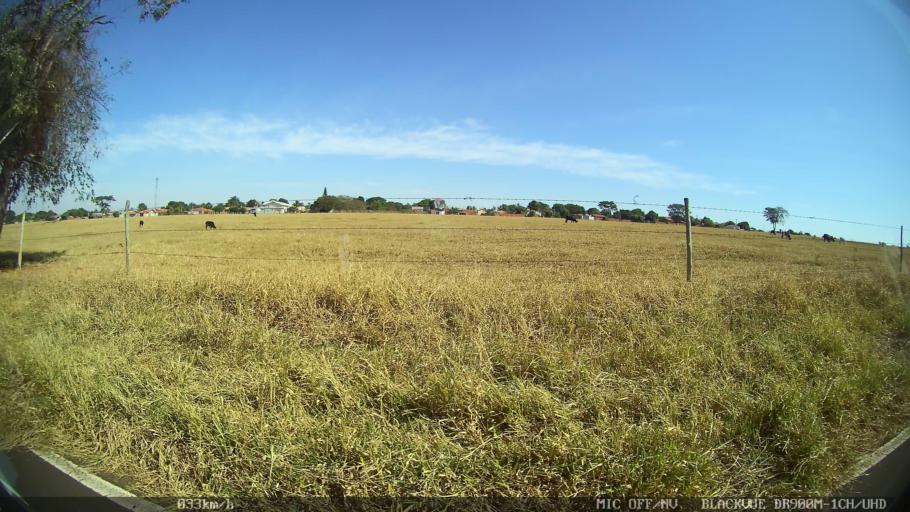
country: BR
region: Sao Paulo
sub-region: Sao Jose Do Rio Preto
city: Sao Jose do Rio Preto
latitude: -20.7500
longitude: -49.4256
